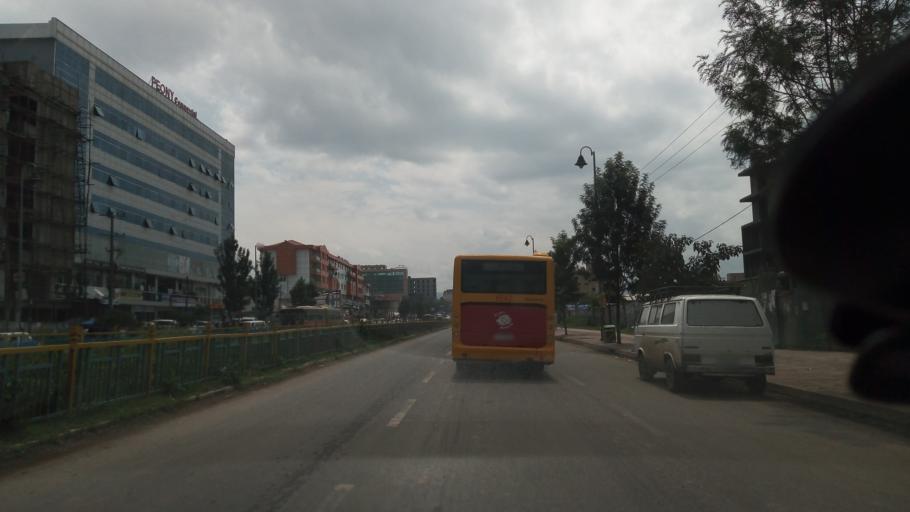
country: ET
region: Adis Abeba
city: Addis Ababa
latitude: 8.9654
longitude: 38.7200
